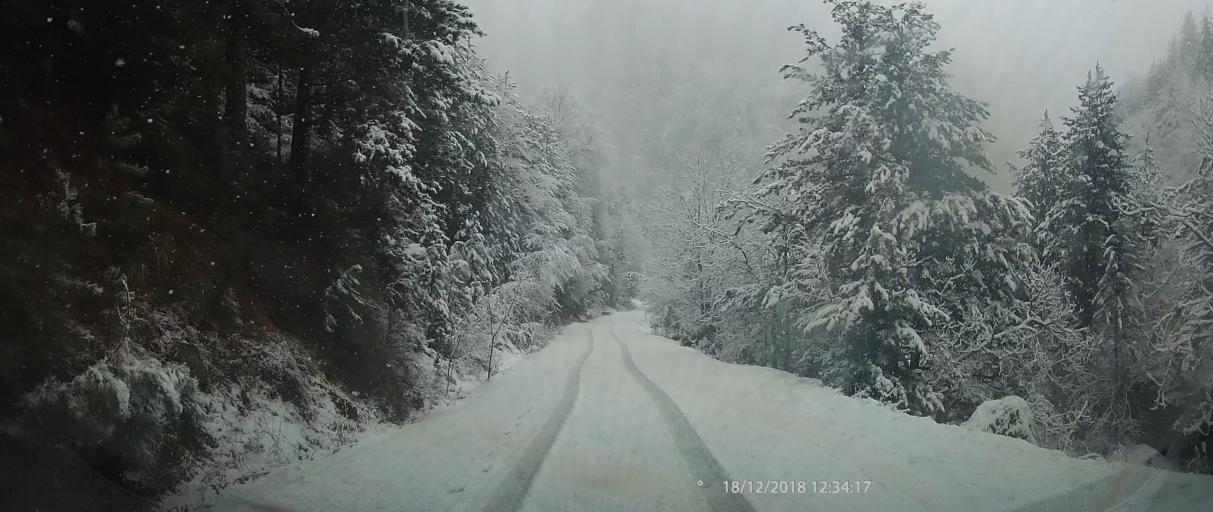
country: GR
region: Central Macedonia
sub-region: Nomos Pierias
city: Litochoro
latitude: 40.0846
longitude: 22.4069
